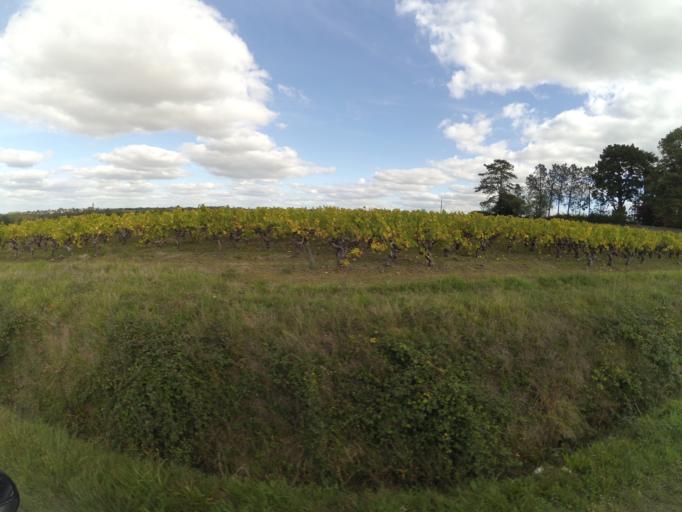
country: FR
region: Pays de la Loire
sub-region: Departement de la Loire-Atlantique
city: Le Loroux-Bottereau
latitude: 47.2170
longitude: -1.3587
